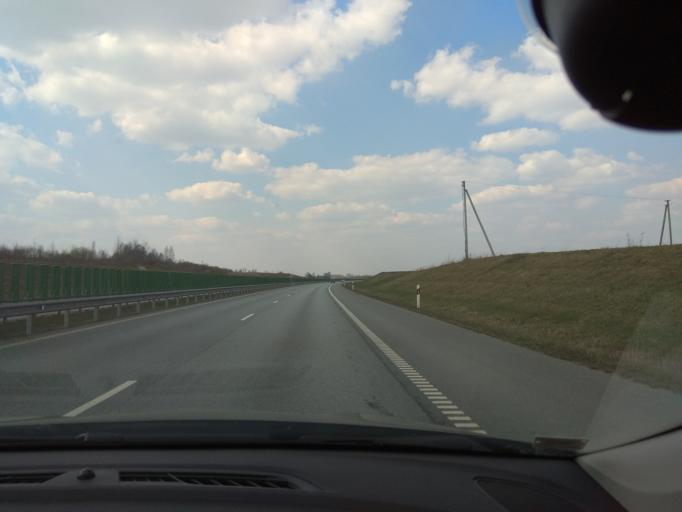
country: LT
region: Siauliu apskritis
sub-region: Siauliai
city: Siauliai
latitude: 55.9075
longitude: 23.4157
